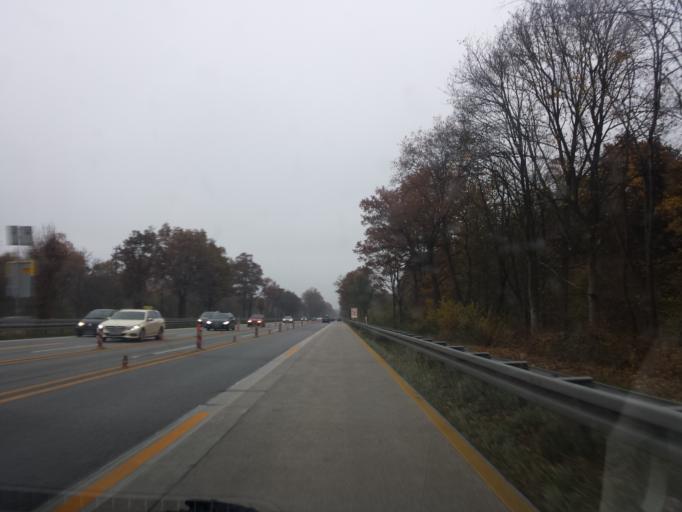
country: DE
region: Bavaria
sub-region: Upper Bavaria
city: Neuried
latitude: 48.0743
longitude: 11.4847
